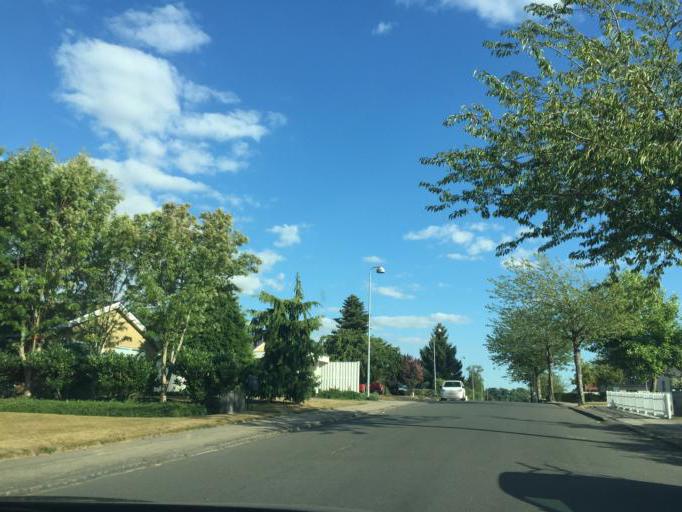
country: DK
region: South Denmark
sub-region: Odense Kommune
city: Odense
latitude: 55.3720
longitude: 10.3533
